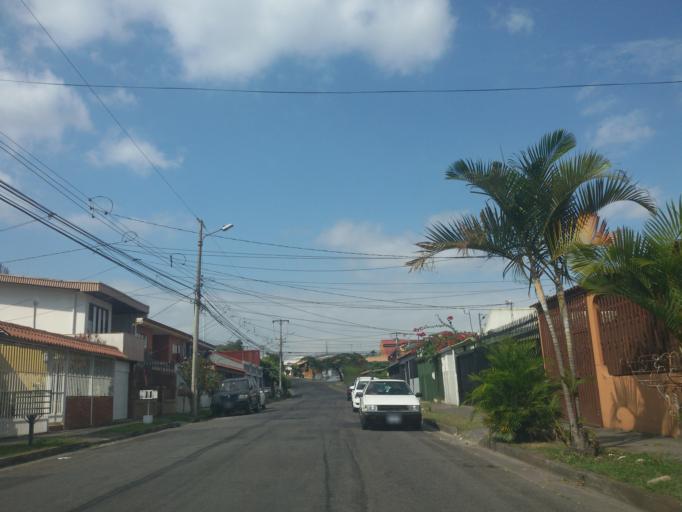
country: CR
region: San Jose
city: Curridabat
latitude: 9.9085
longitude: -84.0359
